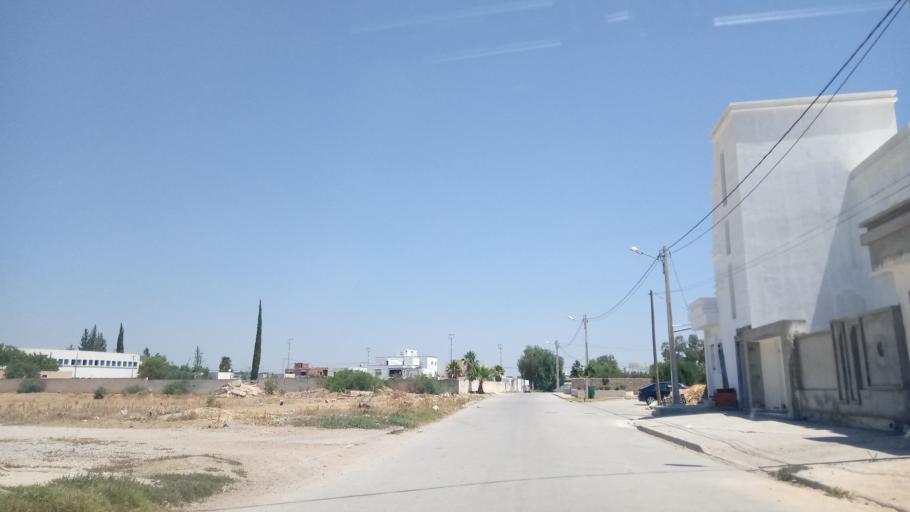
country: TN
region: Al Qayrawan
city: Sbikha
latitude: 36.1187
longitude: 10.0891
